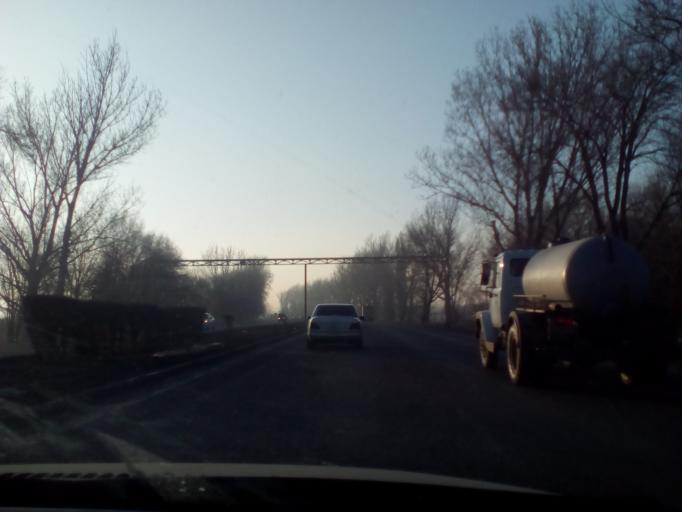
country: KZ
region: Almaty Oblysy
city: Burunday
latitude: 43.2234
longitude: 76.6097
